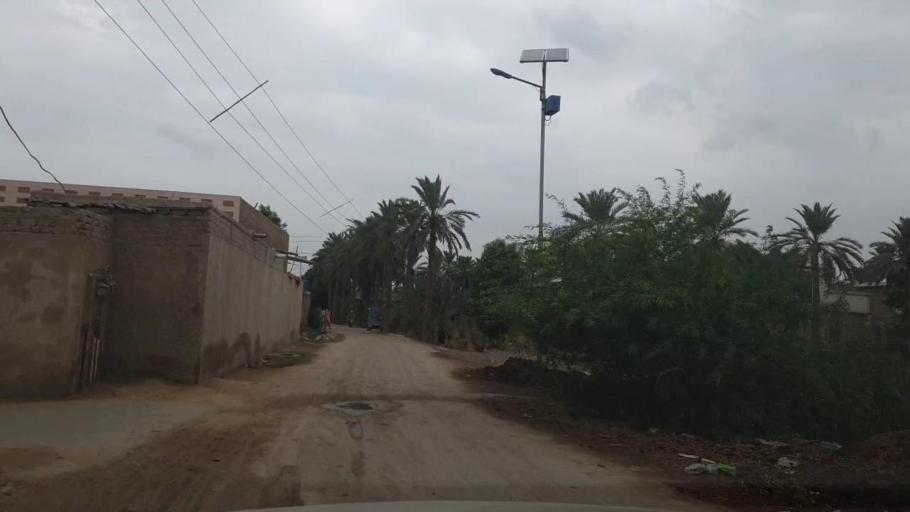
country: PK
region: Sindh
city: Khairpur
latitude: 27.5509
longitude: 68.7509
